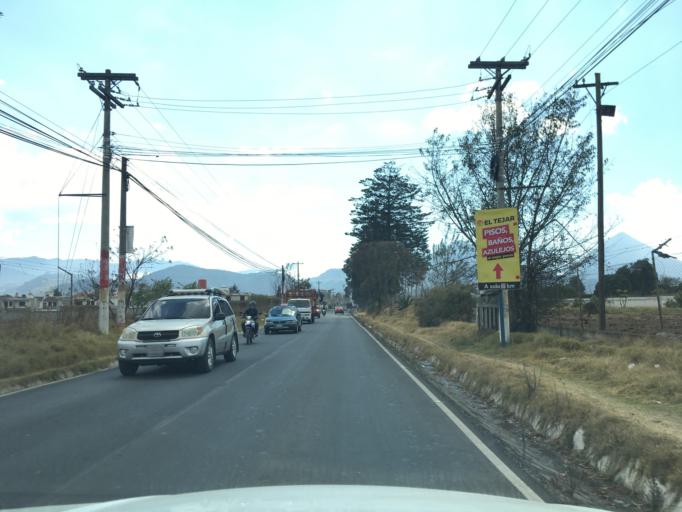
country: GT
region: Quetzaltenango
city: Olintepeque
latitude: 14.8703
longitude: -91.5131
